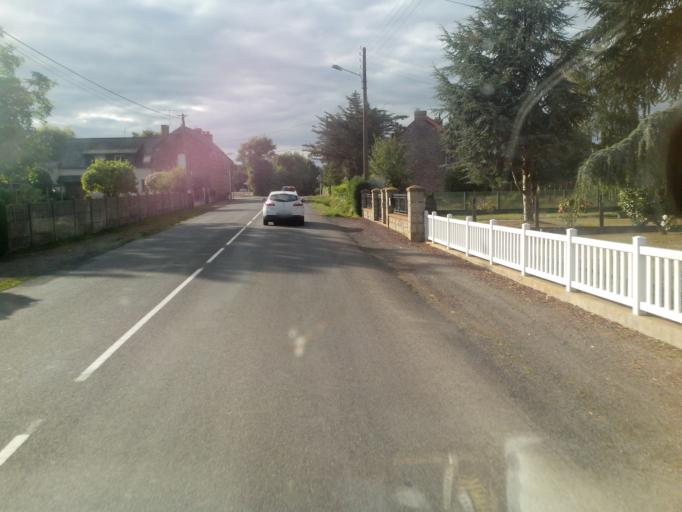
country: FR
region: Brittany
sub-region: Departement d'Ille-et-Vilaine
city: Paimpont
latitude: 48.0655
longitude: -2.1884
